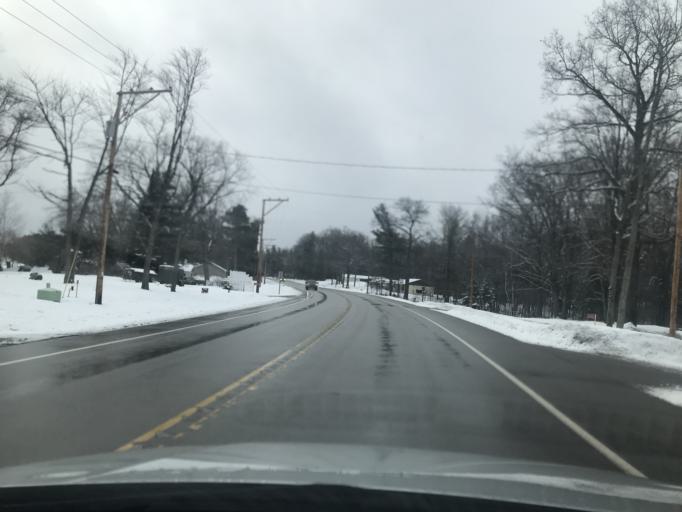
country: US
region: Wisconsin
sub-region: Marinette County
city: Peshtigo
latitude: 45.1723
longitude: -87.7383
